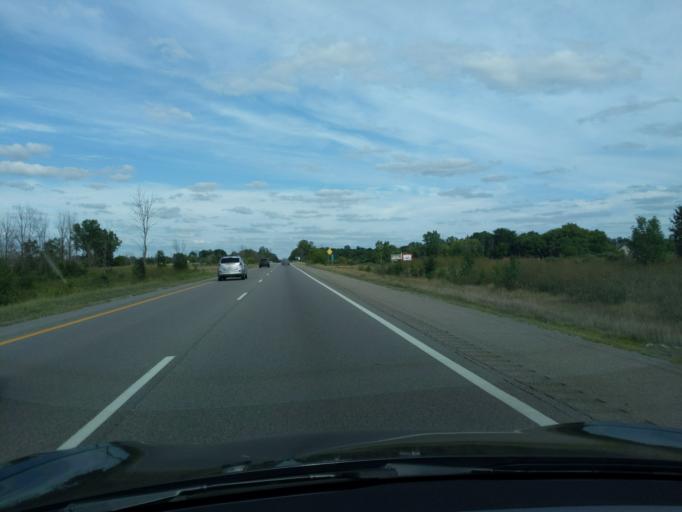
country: US
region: Michigan
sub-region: Ottawa County
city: Coopersville
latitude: 43.0699
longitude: -86.0115
